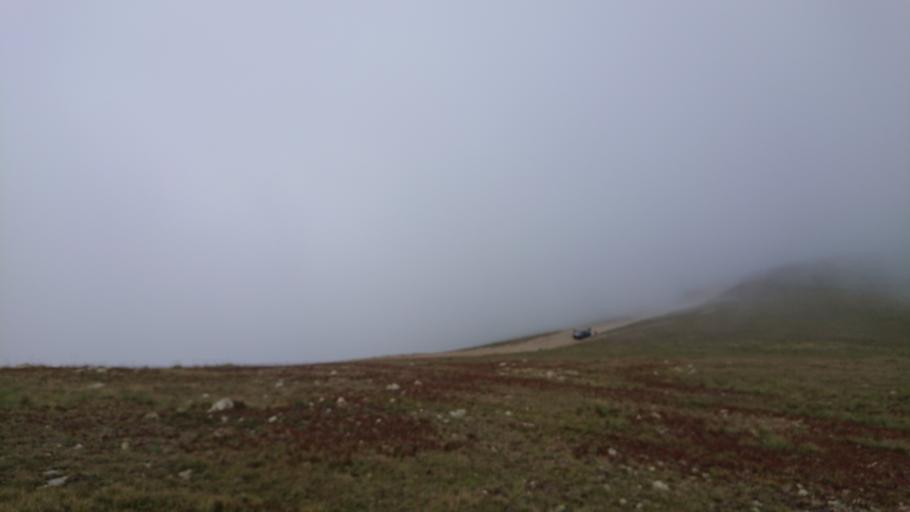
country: TR
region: Gumushane
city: Kurtun
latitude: 40.6227
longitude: 38.9931
